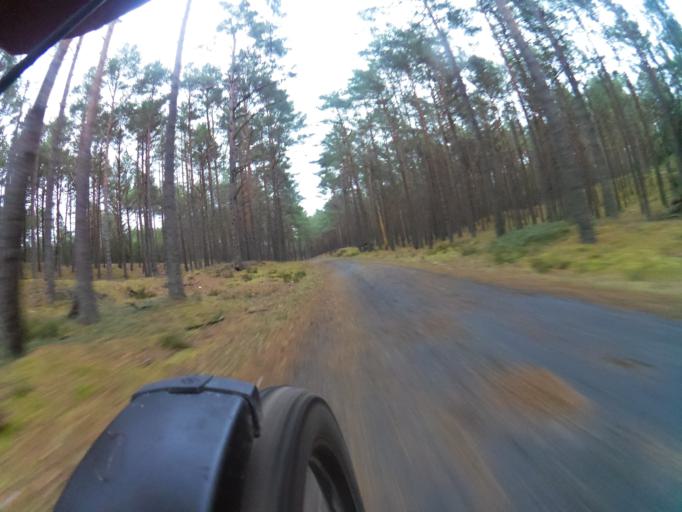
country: PL
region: Pomeranian Voivodeship
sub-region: Powiat wejherowski
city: Choczewo
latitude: 54.7882
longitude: 17.7522
